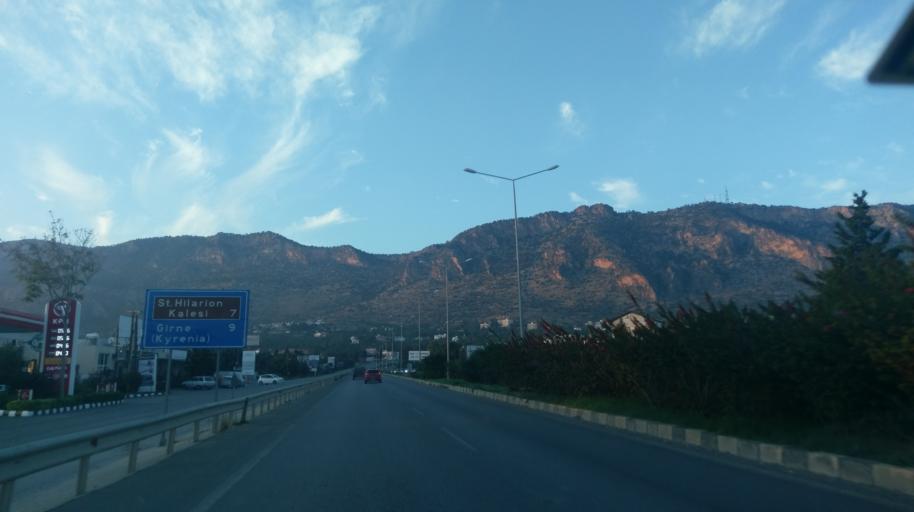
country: CY
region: Keryneia
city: Kyrenia
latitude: 35.2858
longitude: 33.2790
